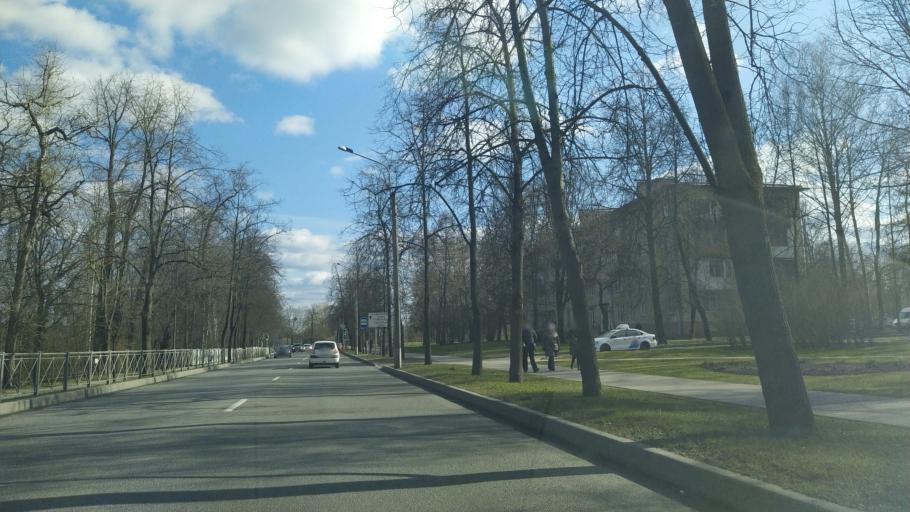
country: RU
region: St.-Petersburg
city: Pushkin
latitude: 59.7049
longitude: 30.4182
